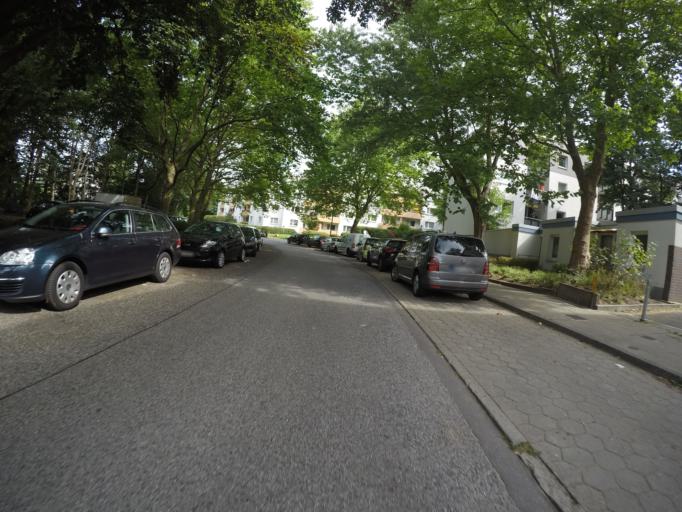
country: DE
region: Hamburg
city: Eidelstedt
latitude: 53.6245
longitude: 9.9135
